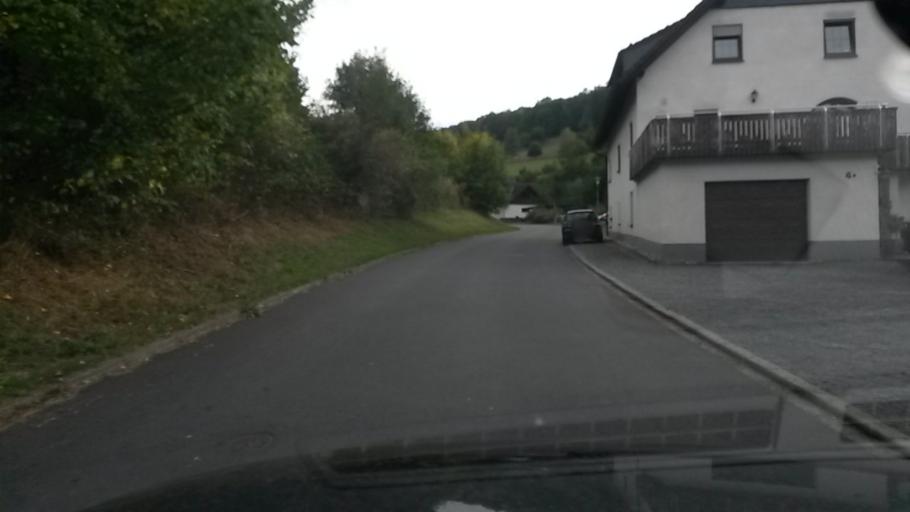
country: DE
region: North Rhine-Westphalia
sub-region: Regierungsbezirk Arnsberg
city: Herscheid
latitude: 51.2218
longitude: 7.7322
